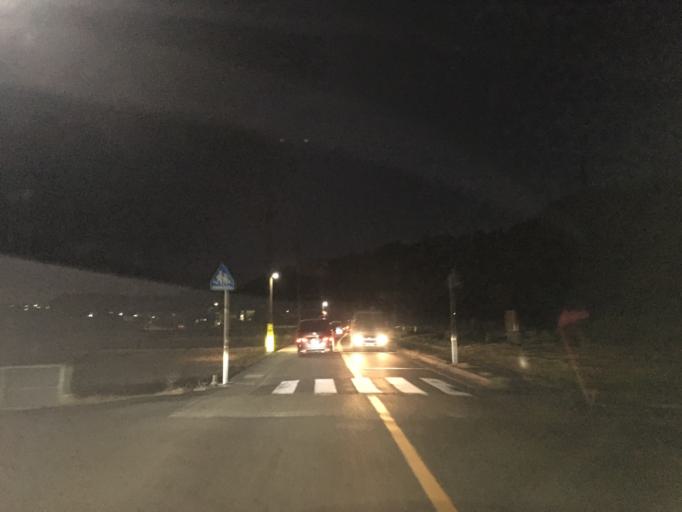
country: JP
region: Tokyo
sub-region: Machida-shi
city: Machida
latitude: 35.5729
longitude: 139.5149
